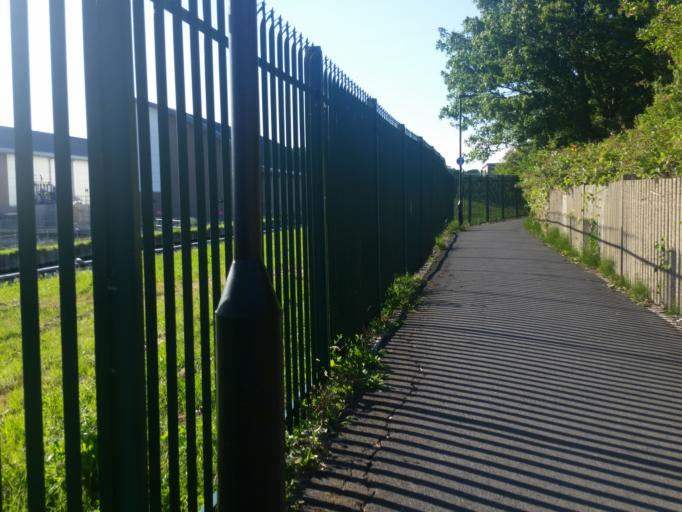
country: GB
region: England
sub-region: Greater London
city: Wood Green
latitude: 51.5922
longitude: -0.1163
